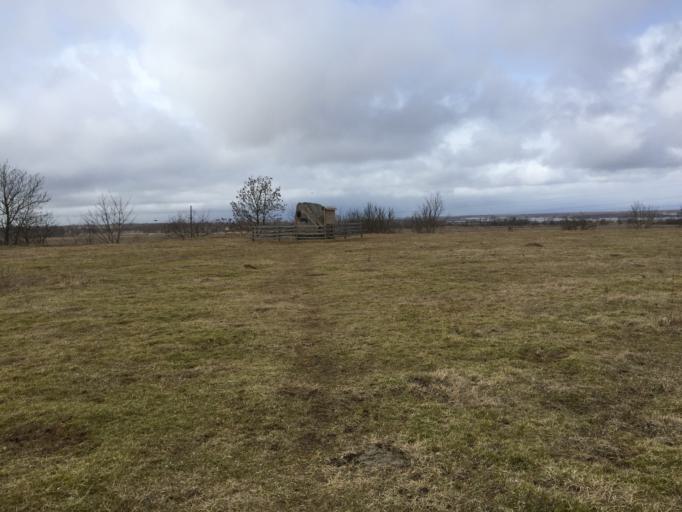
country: EE
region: Laeaene
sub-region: Lihula vald
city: Lihula
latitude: 58.7279
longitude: 23.9278
